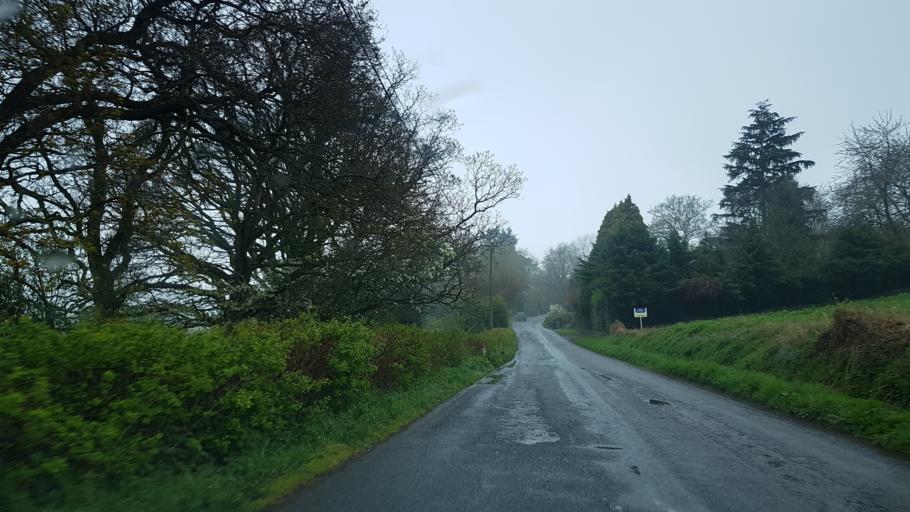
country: GB
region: England
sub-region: Herefordshire
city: Ledbury
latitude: 52.0587
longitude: -2.4261
